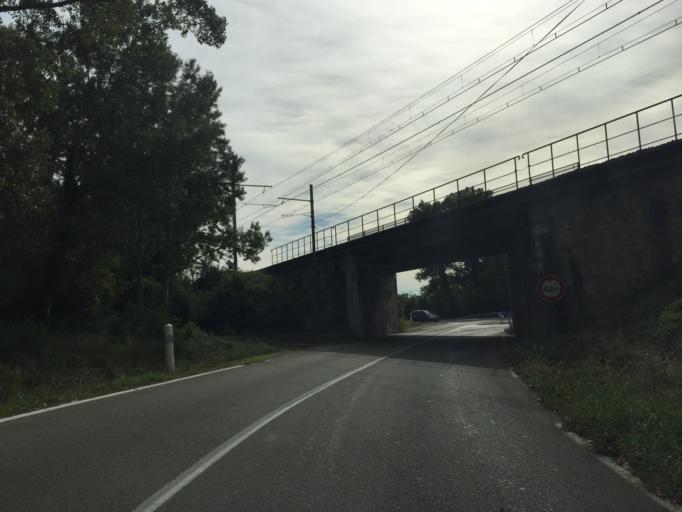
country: FR
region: Provence-Alpes-Cote d'Azur
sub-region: Departement du Vaucluse
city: Mondragon
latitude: 44.2280
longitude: 4.7138
